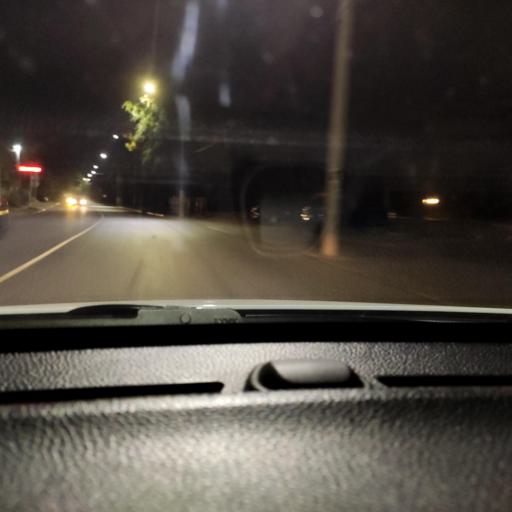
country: RU
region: Voronezj
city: Voronezh
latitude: 51.7317
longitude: 39.2600
